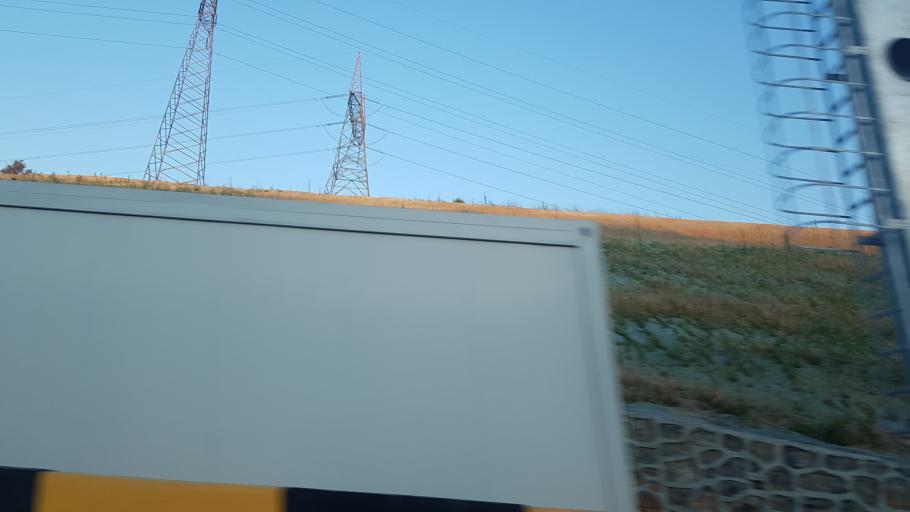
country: TR
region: Kocaeli
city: Tavsanli
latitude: 40.8053
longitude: 29.5199
